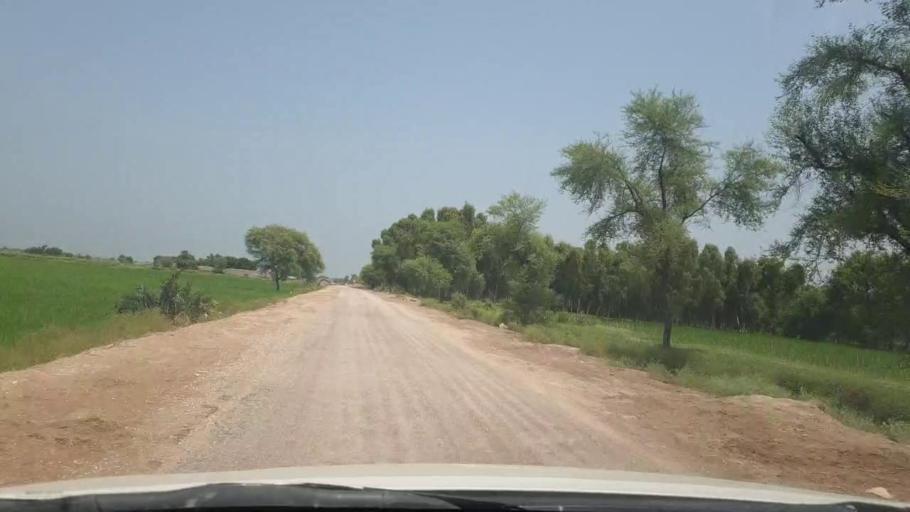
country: PK
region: Sindh
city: Rustam jo Goth
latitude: 28.0290
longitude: 68.7789
